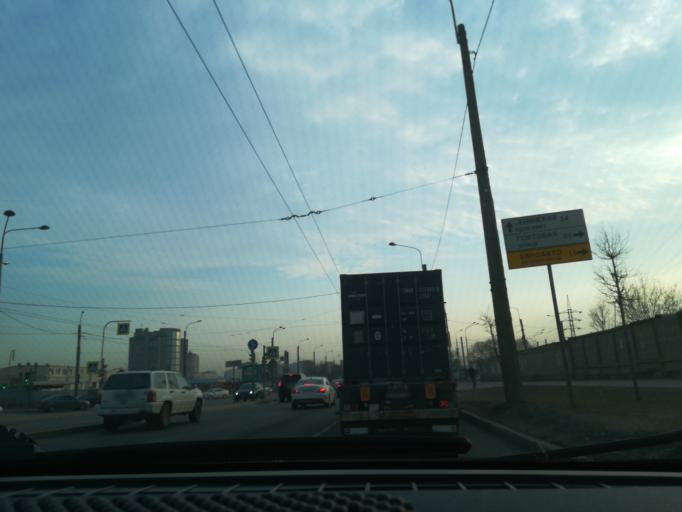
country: RU
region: St.-Petersburg
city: Avtovo
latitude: 59.8696
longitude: 30.2473
